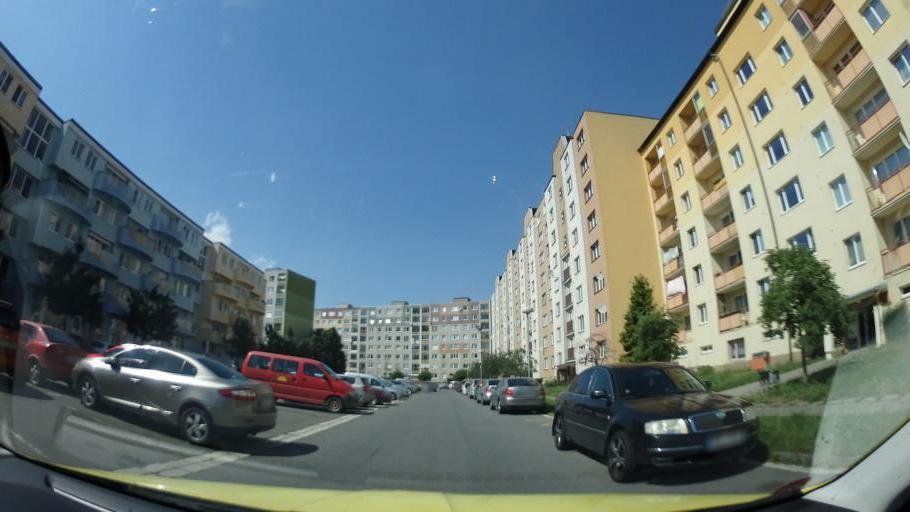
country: CZ
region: Olomoucky
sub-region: Okres Olomouc
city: Olomouc
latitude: 49.5714
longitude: 17.2556
